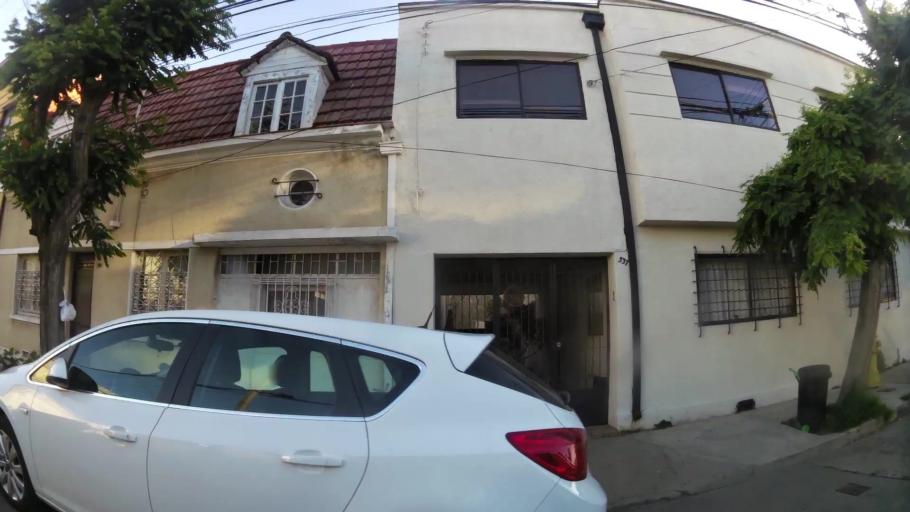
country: CL
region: Valparaiso
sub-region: Provincia de Valparaiso
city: Vina del Mar
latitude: -33.0230
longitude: -71.5661
